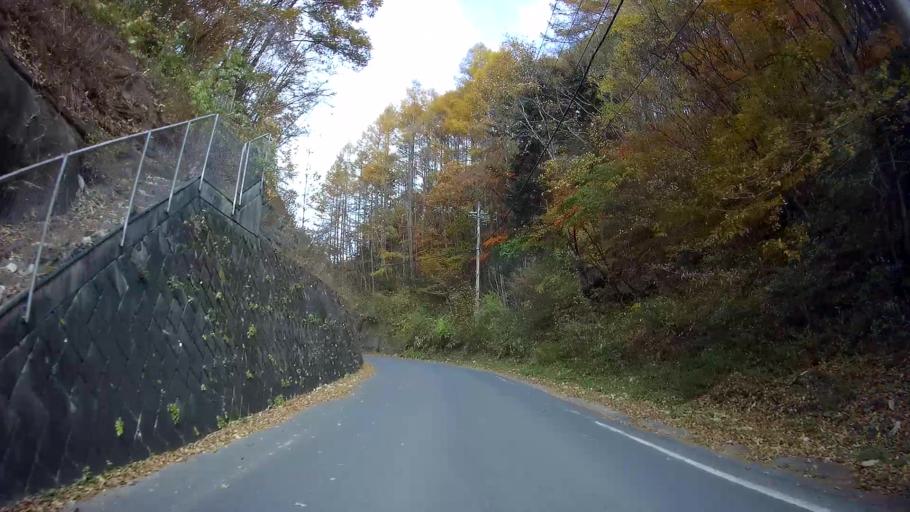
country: JP
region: Gunma
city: Nakanojomachi
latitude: 36.6316
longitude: 138.6361
